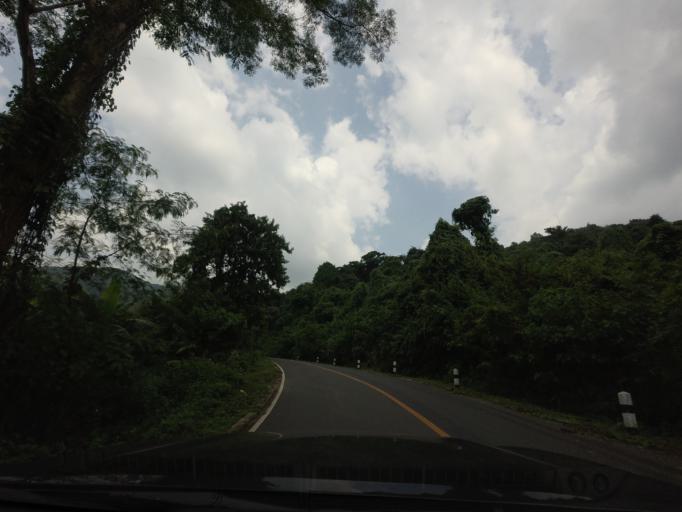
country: TH
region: Nan
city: Pua
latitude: 19.1795
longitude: 100.9712
